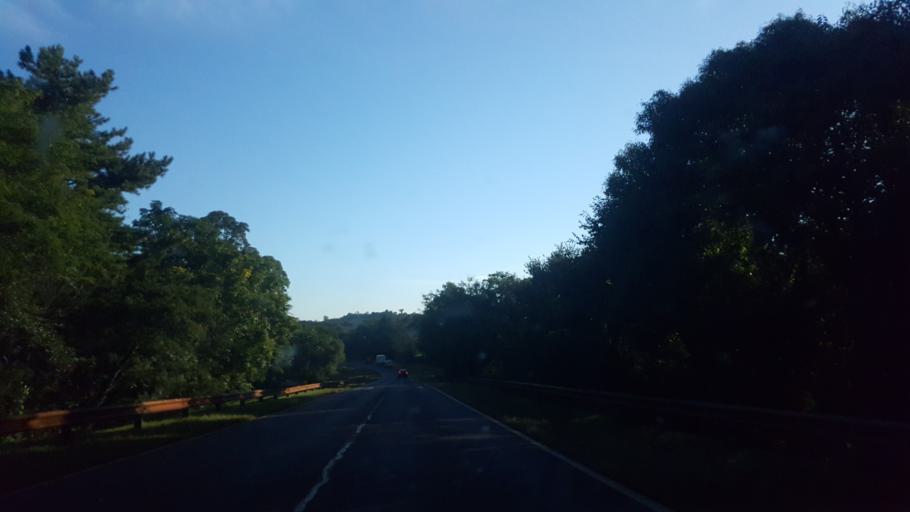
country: AR
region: Misiones
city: El Alcazar
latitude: -26.7313
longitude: -54.8727
